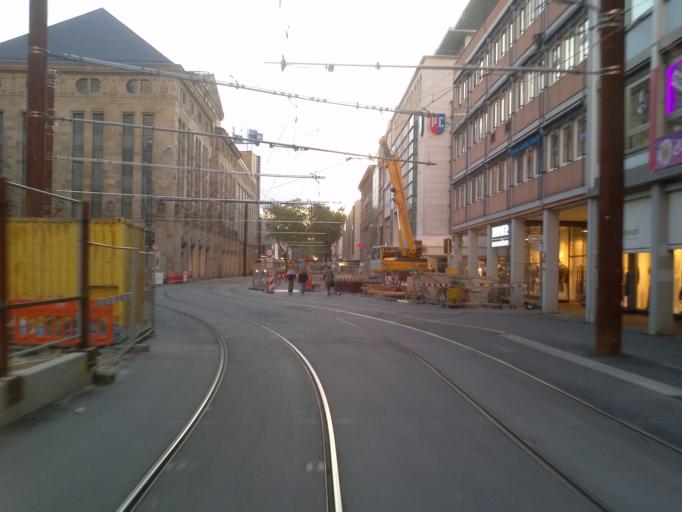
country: DE
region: Baden-Wuerttemberg
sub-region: Karlsruhe Region
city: Karlsruhe
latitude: 49.0095
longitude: 8.4029
